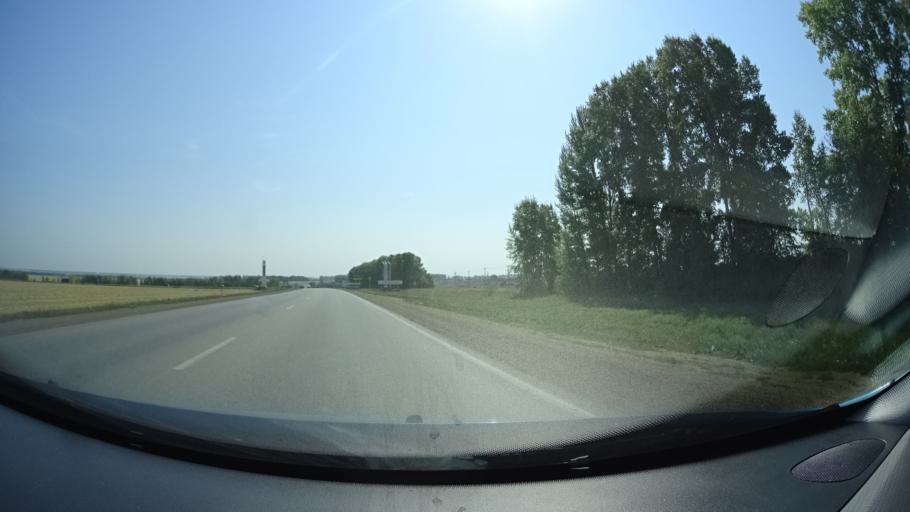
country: RU
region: Bashkortostan
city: Kabakovo
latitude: 54.4702
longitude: 55.9462
